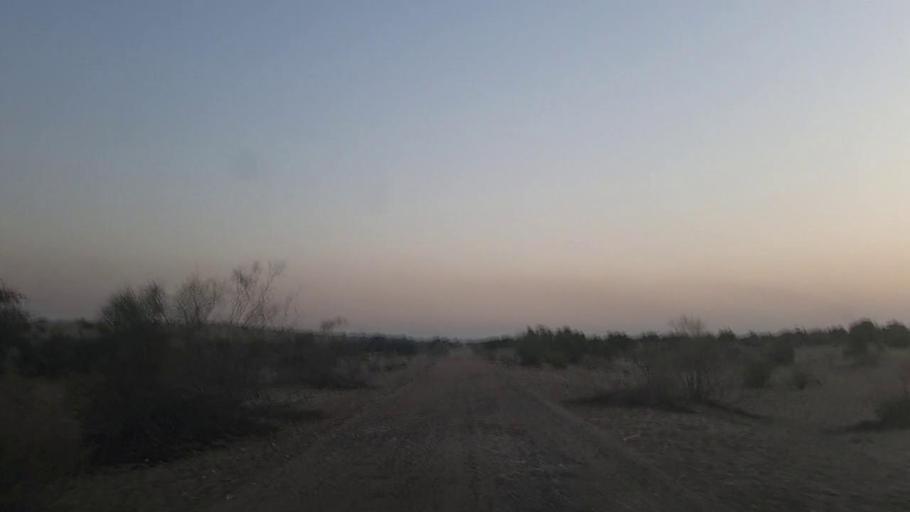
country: PK
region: Sindh
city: Jam Sahib
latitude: 26.4028
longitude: 68.8097
